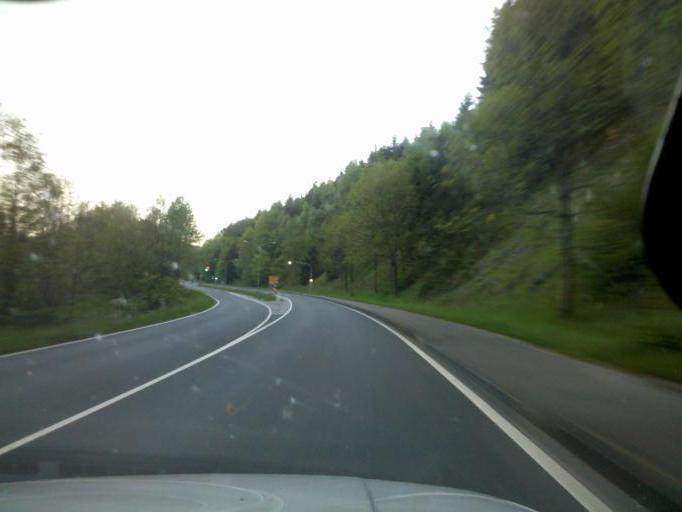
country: DE
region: North Rhine-Westphalia
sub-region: Regierungsbezirk Koln
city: Gummersbach
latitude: 50.9965
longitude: 7.5498
